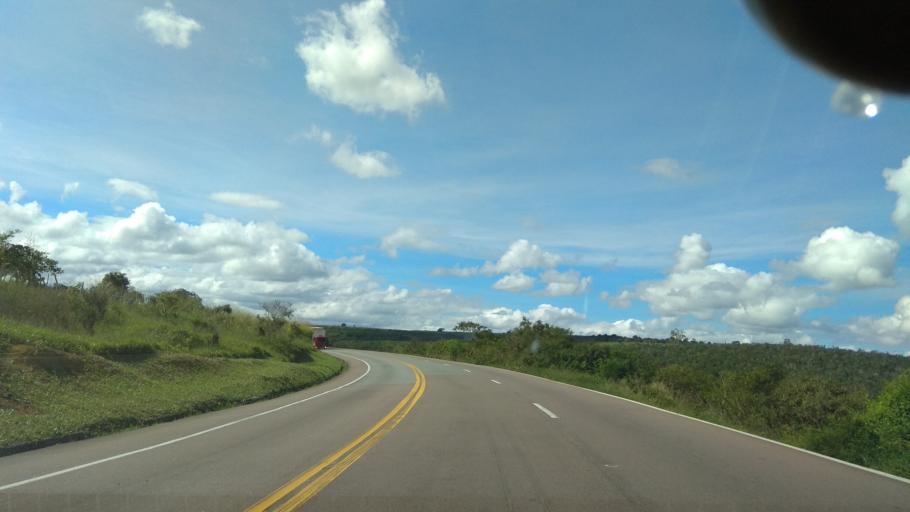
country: BR
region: Bahia
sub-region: Santa Ines
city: Santa Ines
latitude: -13.2109
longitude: -40.0191
